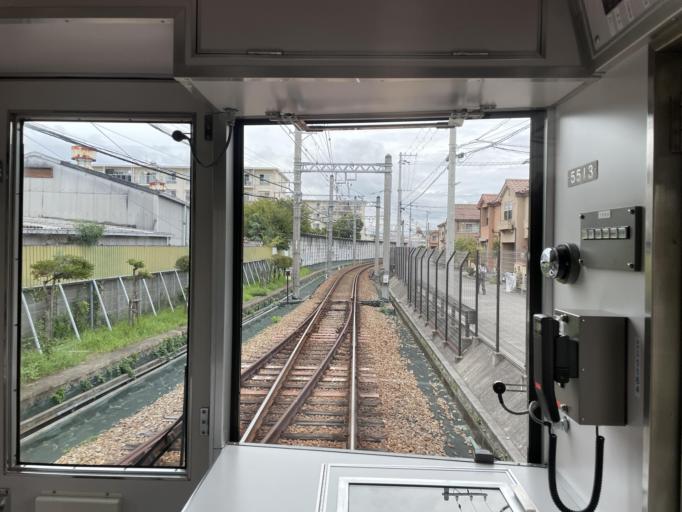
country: JP
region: Hyogo
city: Amagasaki
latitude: 34.7054
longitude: 135.3751
